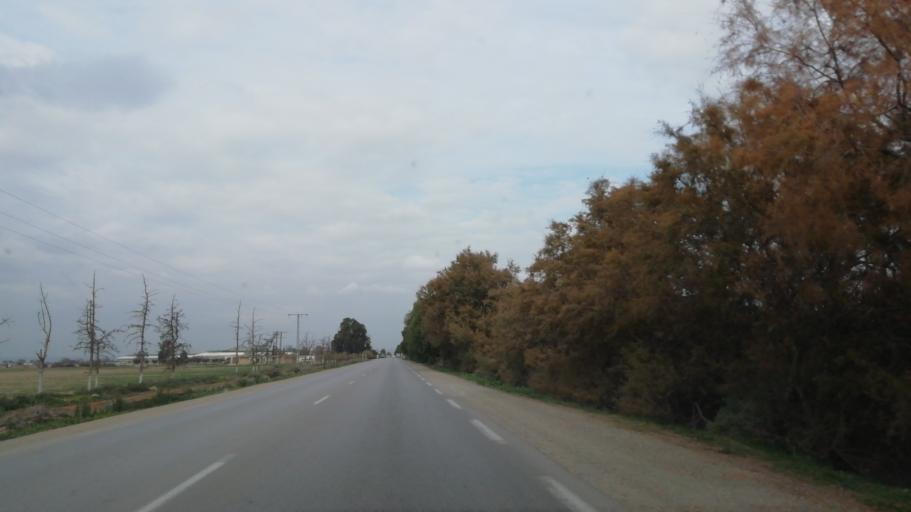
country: DZ
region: Mascara
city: Mascara
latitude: 35.6515
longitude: 0.0595
